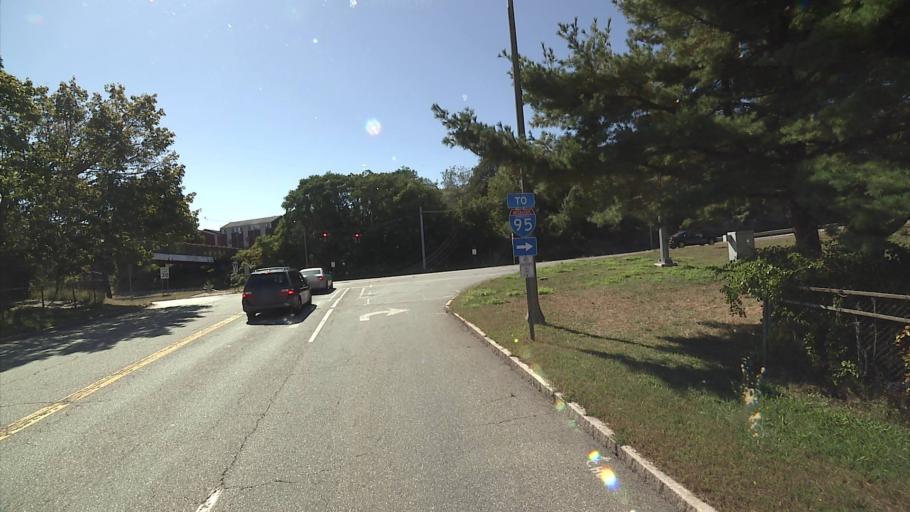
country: US
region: Connecticut
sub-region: New London County
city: New London
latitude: 41.3605
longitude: -72.0982
